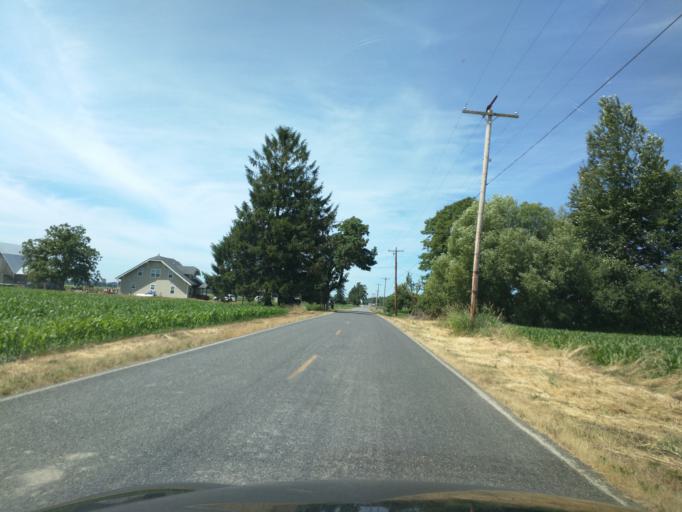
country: US
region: Washington
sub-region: Whatcom County
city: Lynden
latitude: 48.9350
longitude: -122.4295
